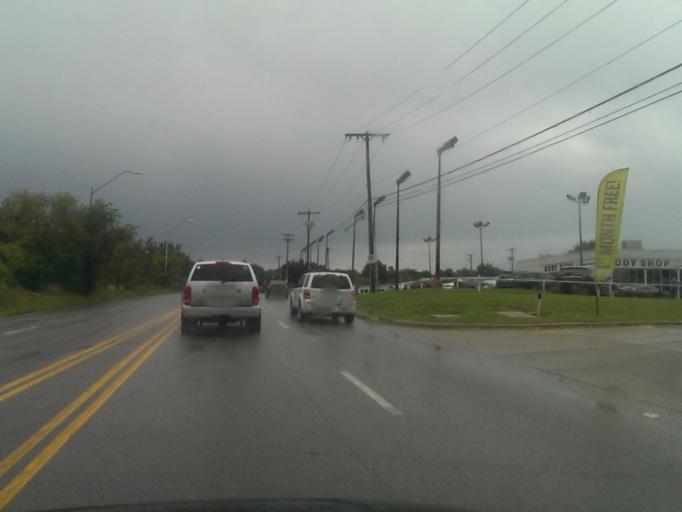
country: US
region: Kansas
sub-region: Johnson County
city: Leawood
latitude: 38.9568
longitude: -94.5819
